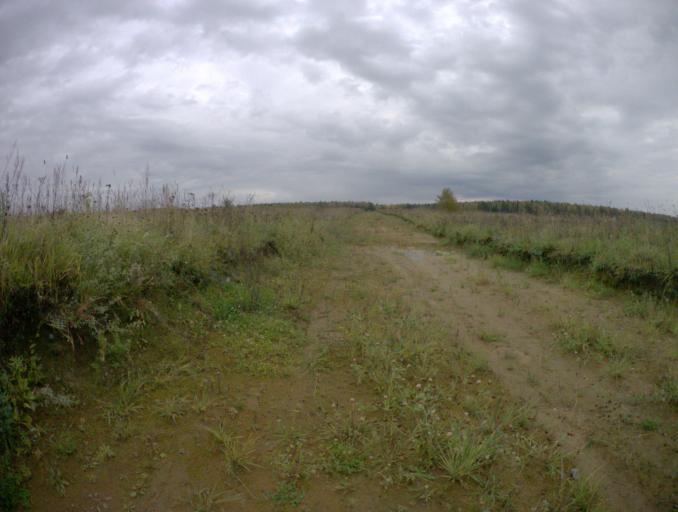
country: RU
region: Vladimir
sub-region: Kovrovskiy Rayon
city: Kovrov
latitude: 56.3511
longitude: 41.4460
